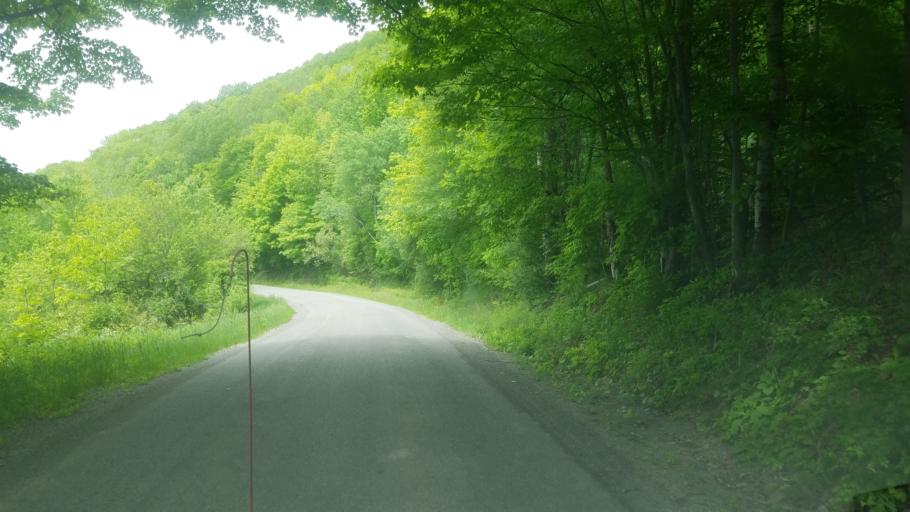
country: US
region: Pennsylvania
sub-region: Tioga County
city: Westfield
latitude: 41.8923
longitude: -77.6008
